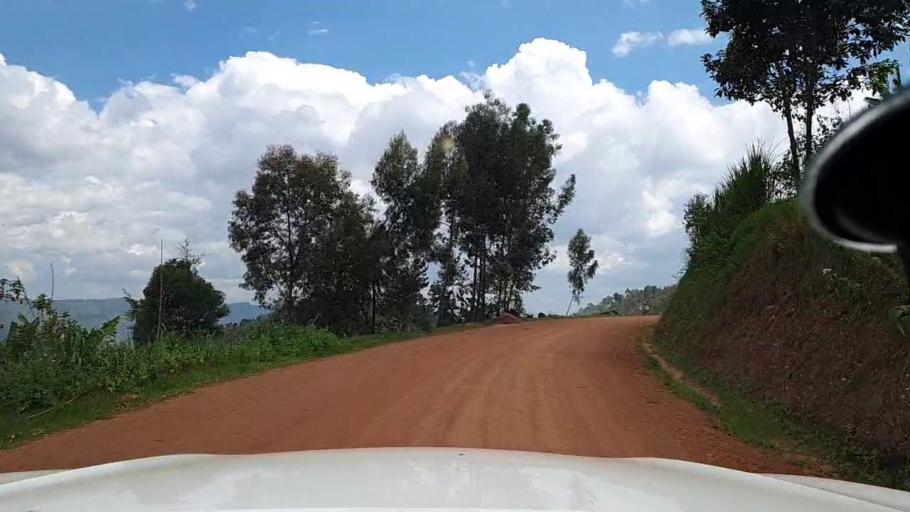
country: RW
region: Kigali
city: Kigali
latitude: -1.7808
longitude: 29.8404
